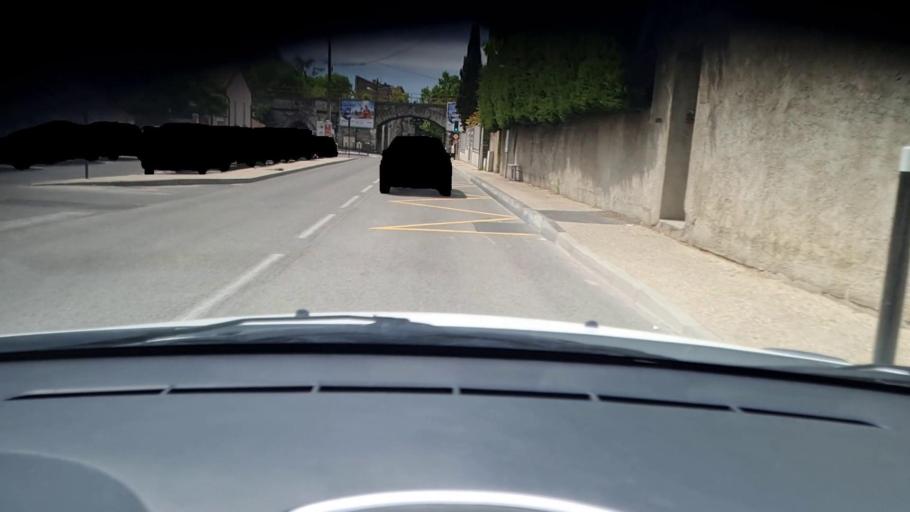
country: FR
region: Languedoc-Roussillon
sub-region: Departement du Gard
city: Nimes
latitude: 43.8499
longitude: 4.3741
